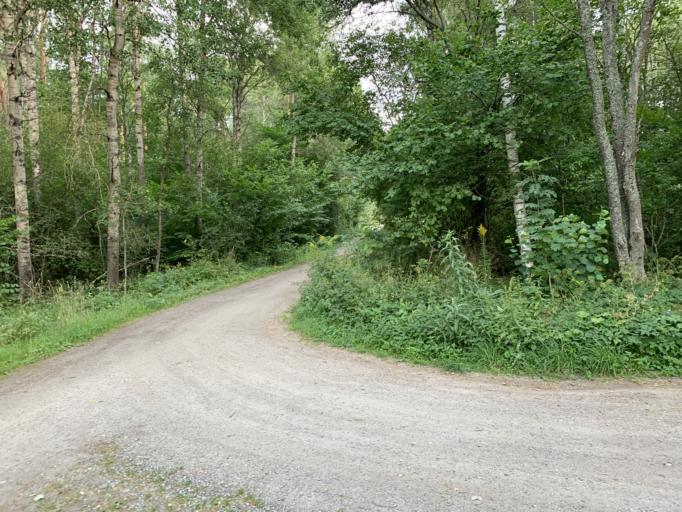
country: SE
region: Stockholm
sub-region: Solna Kommun
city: Rasunda
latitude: 59.3941
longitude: 17.9734
